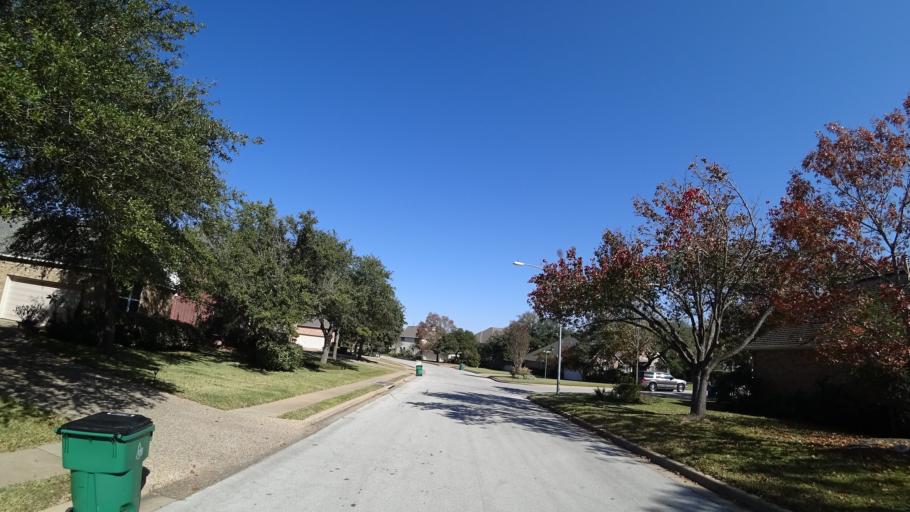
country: US
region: Texas
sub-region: Travis County
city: Lost Creek
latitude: 30.3781
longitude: -97.8518
